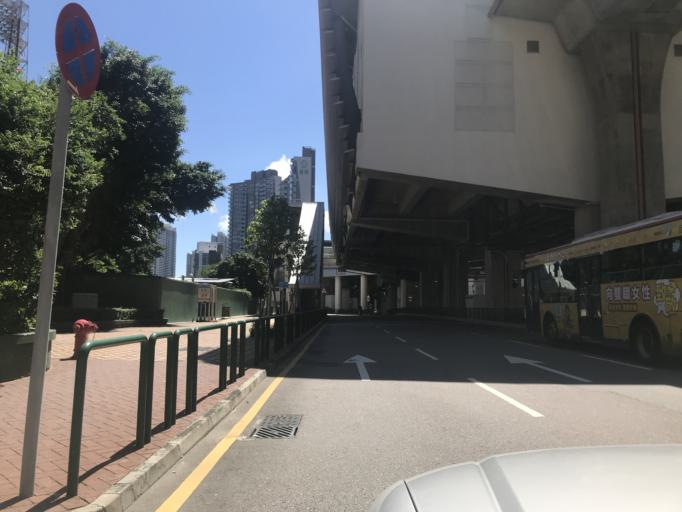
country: MO
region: Macau
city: Macau
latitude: 22.1570
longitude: 113.5478
